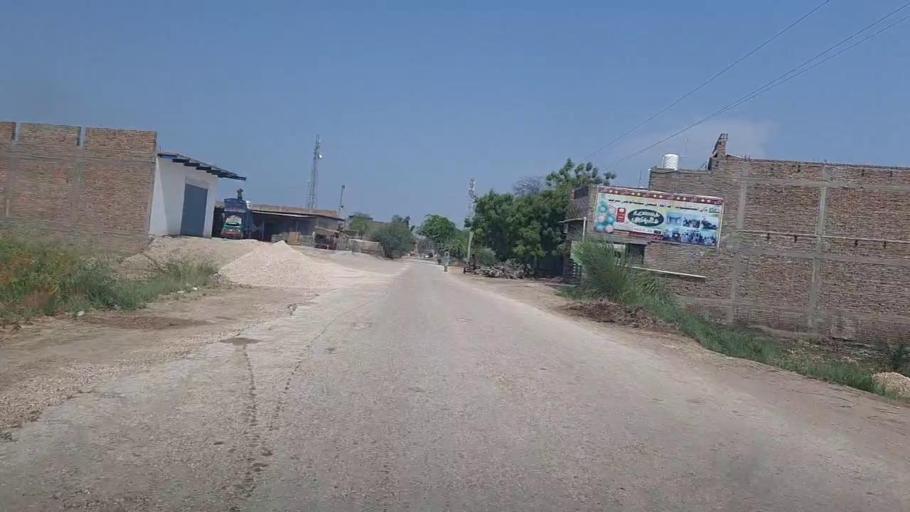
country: PK
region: Sindh
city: Ghotki
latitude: 28.0402
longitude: 69.4138
